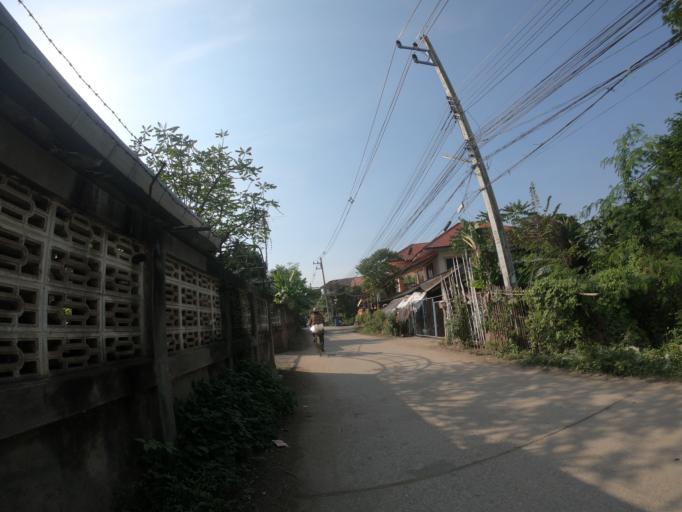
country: TH
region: Chiang Mai
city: Chiang Mai
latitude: 18.7654
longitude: 99.0150
